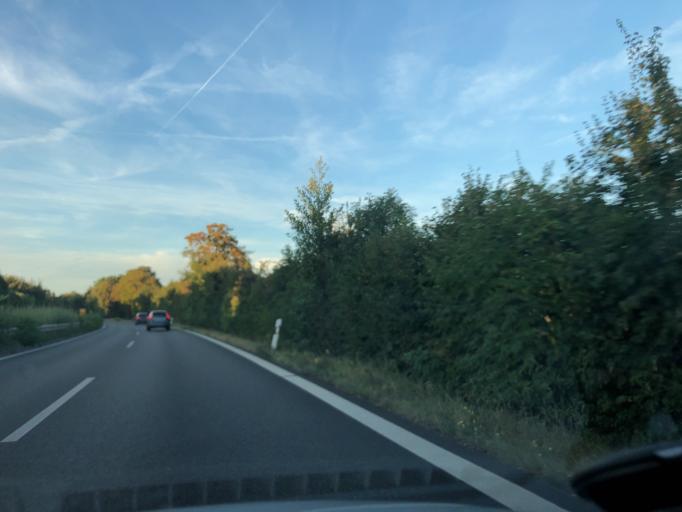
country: DE
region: Baden-Wuerttemberg
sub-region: Regierungsbezirk Stuttgart
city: Kornwestheim
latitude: 48.8548
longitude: 9.1948
